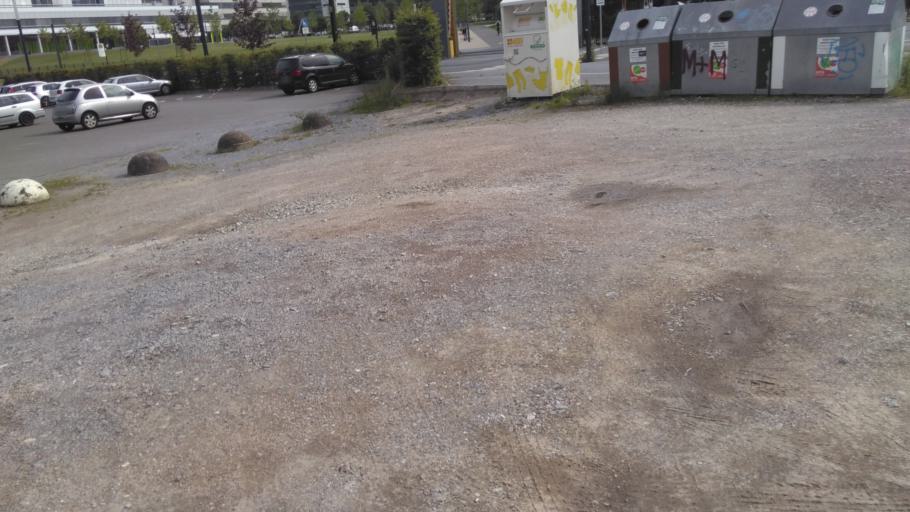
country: DE
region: North Rhine-Westphalia
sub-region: Regierungsbezirk Detmold
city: Bielefeld
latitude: 52.0425
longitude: 8.4910
